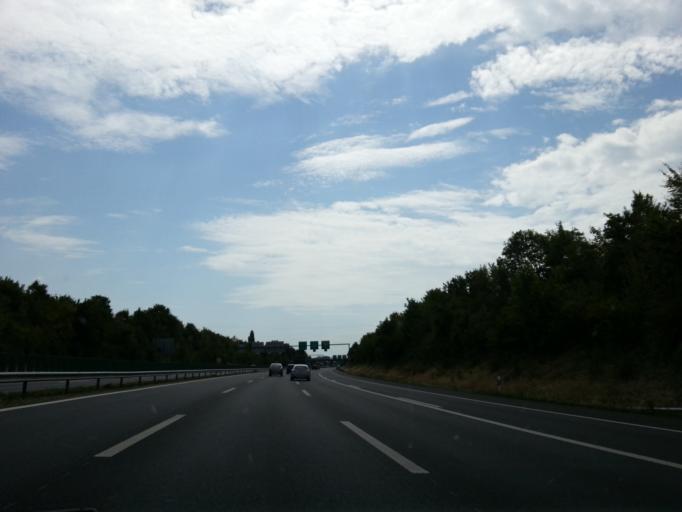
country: CH
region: Geneva
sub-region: Geneva
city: Plan-les-Ouates
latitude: 46.1573
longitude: 6.1009
